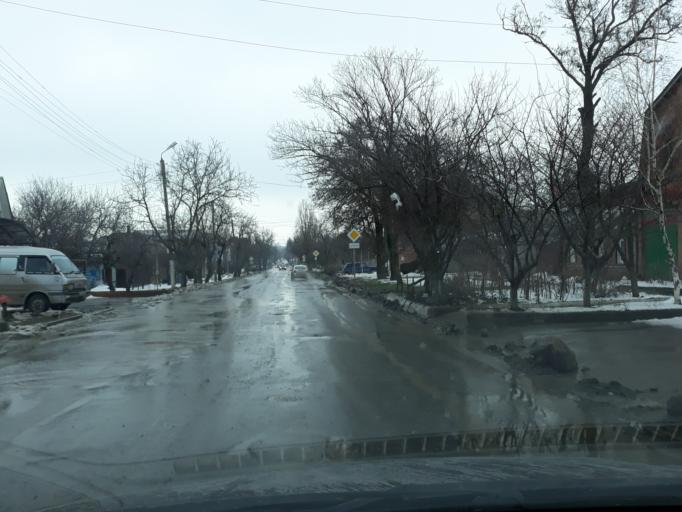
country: RU
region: Rostov
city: Taganrog
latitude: 47.2278
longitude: 38.8971
